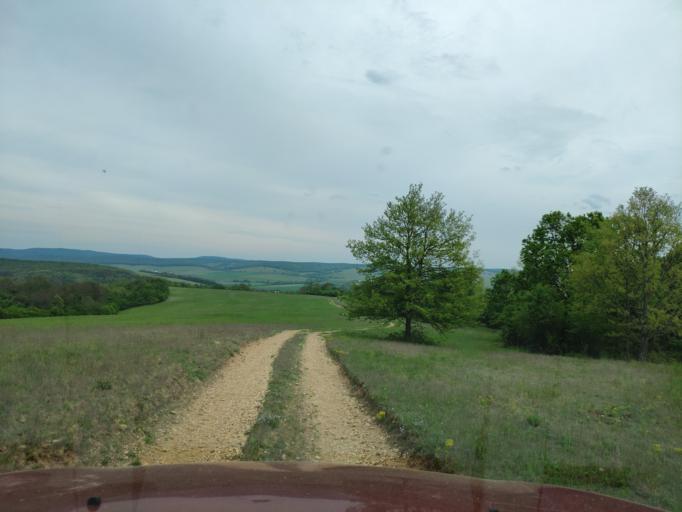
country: HU
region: Borsod-Abauj-Zemplen
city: Putnok
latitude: 48.4921
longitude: 20.3204
